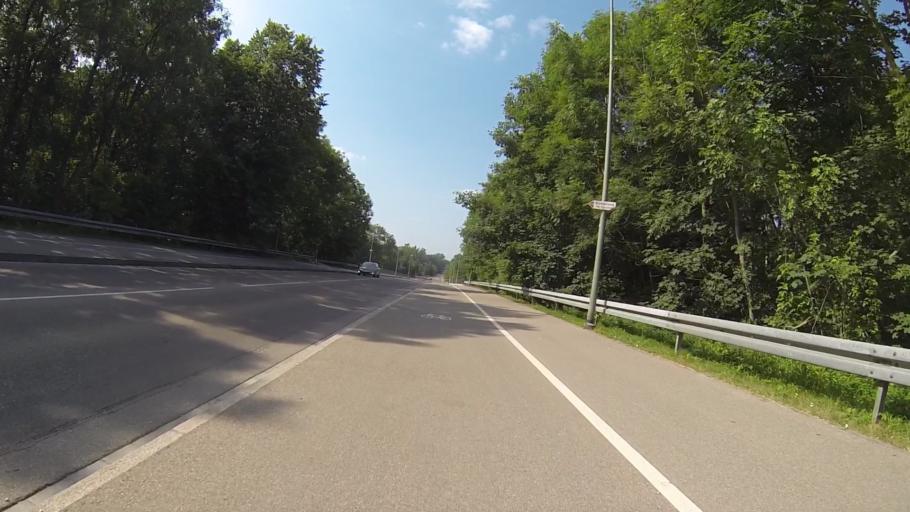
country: DE
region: Bavaria
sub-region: Swabia
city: Guenzburg
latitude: 48.4585
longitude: 10.2700
